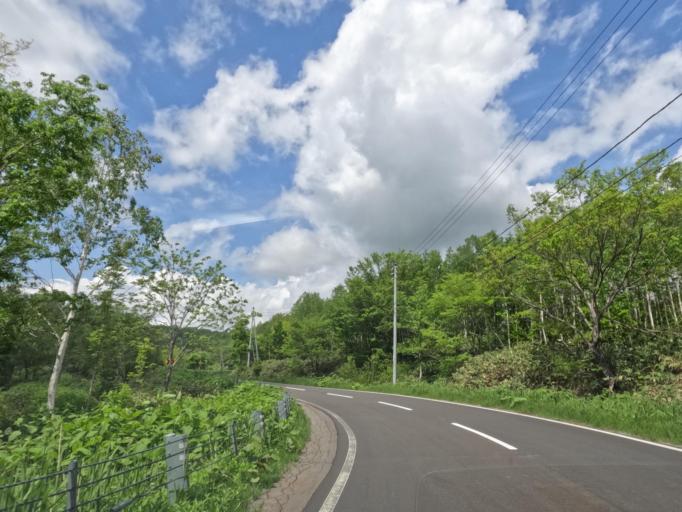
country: JP
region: Hokkaido
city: Takikawa
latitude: 43.5454
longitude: 141.6524
